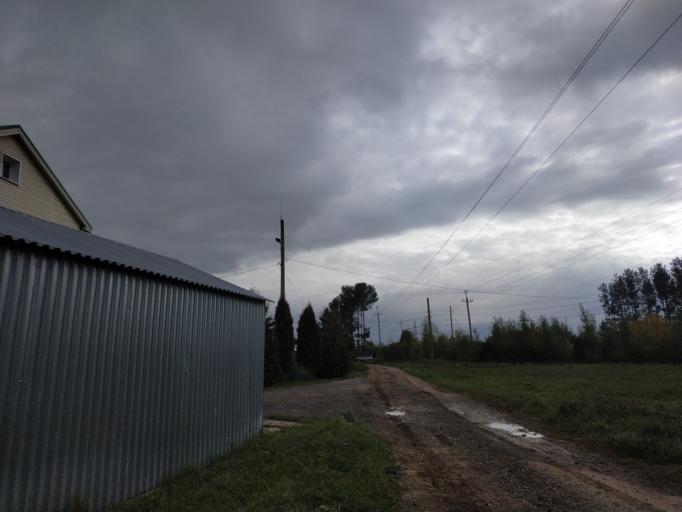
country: RU
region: Chuvashia
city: Ishley
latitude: 56.1289
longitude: 47.0913
